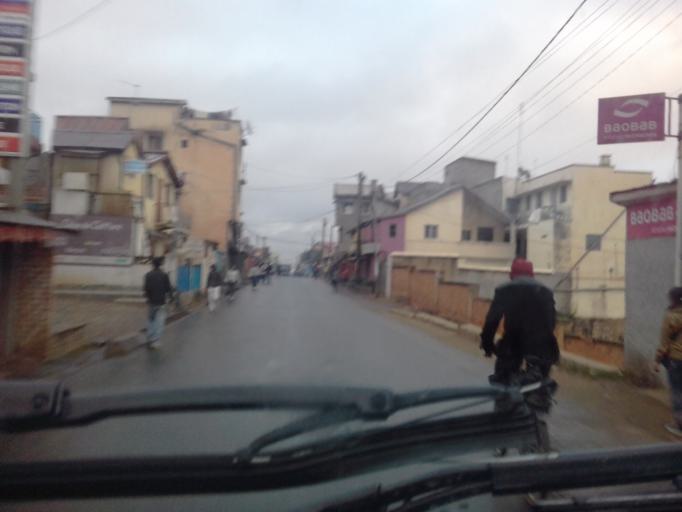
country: MG
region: Analamanga
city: Antananarivo
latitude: -18.8730
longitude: 47.5512
